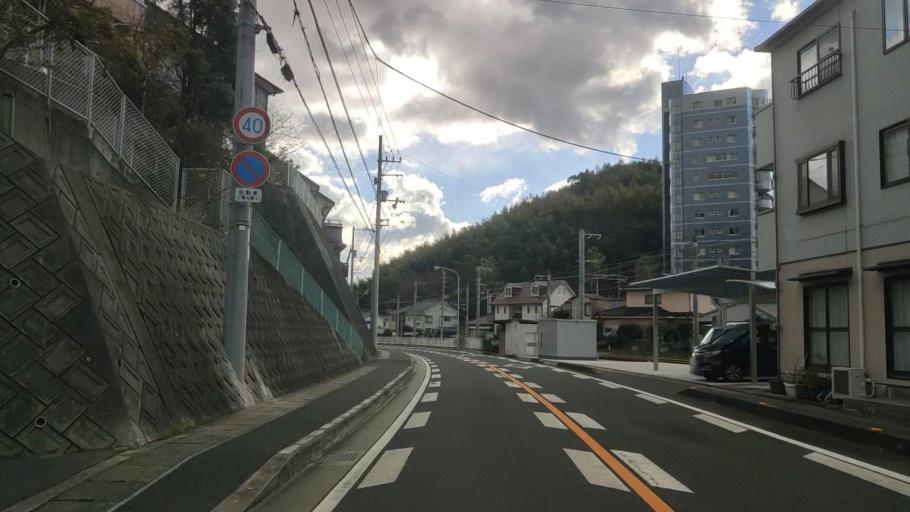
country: JP
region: Ehime
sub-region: Shikoku-chuo Shi
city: Matsuyama
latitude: 33.8706
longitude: 132.7105
